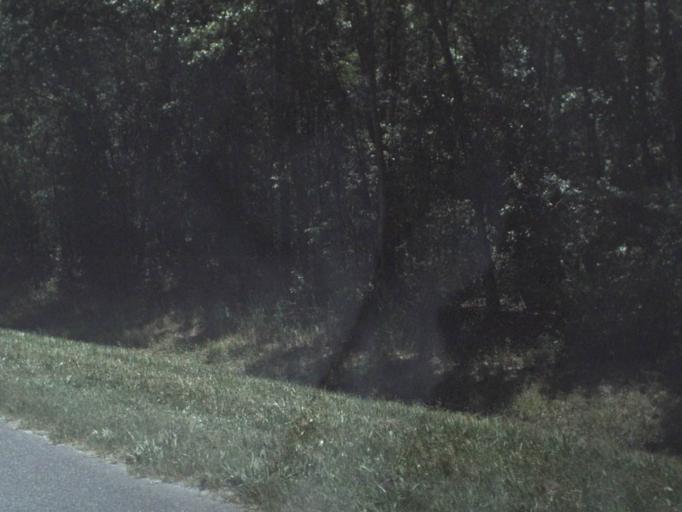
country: US
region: Florida
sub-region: Columbia County
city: Five Points
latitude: 30.2409
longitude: -82.6717
